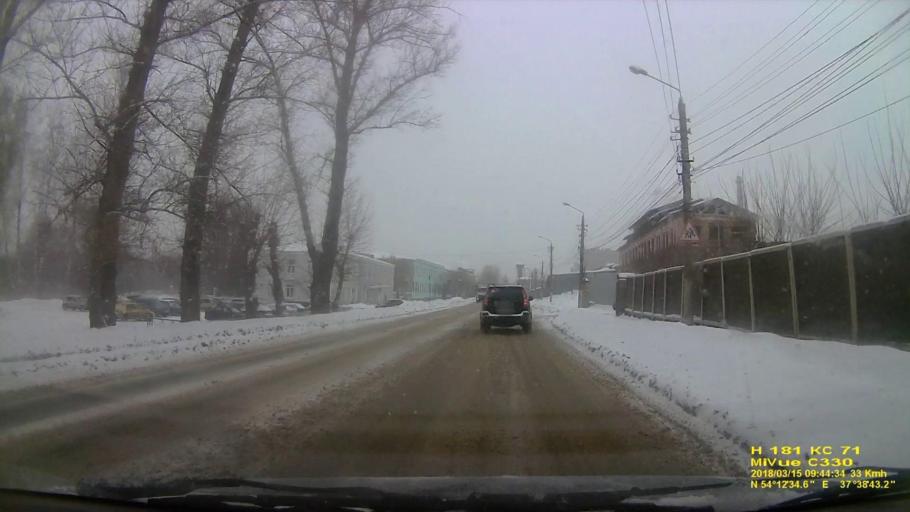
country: RU
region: Tula
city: Tula
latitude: 54.2097
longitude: 37.6454
